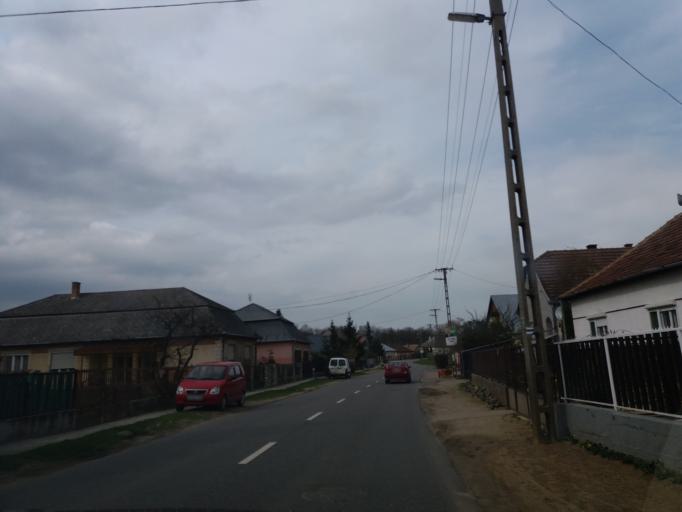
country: HU
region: Szabolcs-Szatmar-Bereg
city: Anarcs
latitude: 48.1711
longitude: 22.0967
